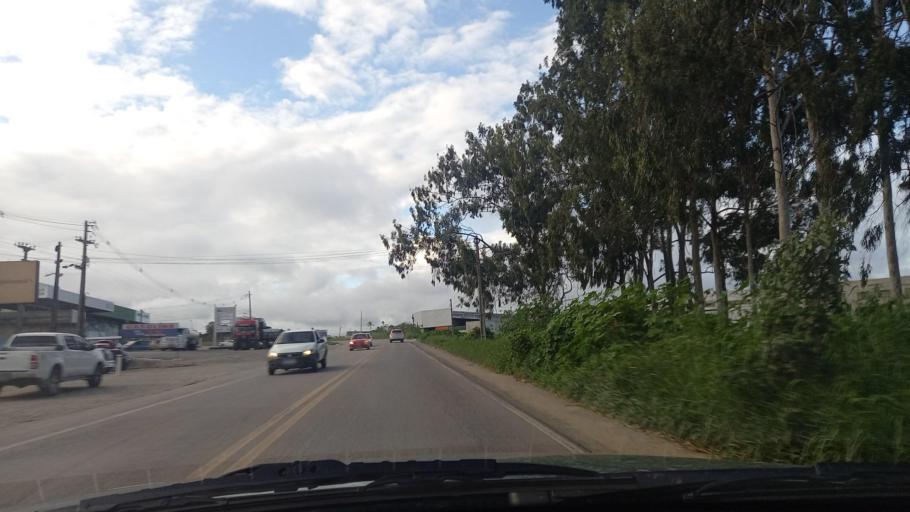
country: BR
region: Pernambuco
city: Garanhuns
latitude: -8.9102
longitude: -36.4875
